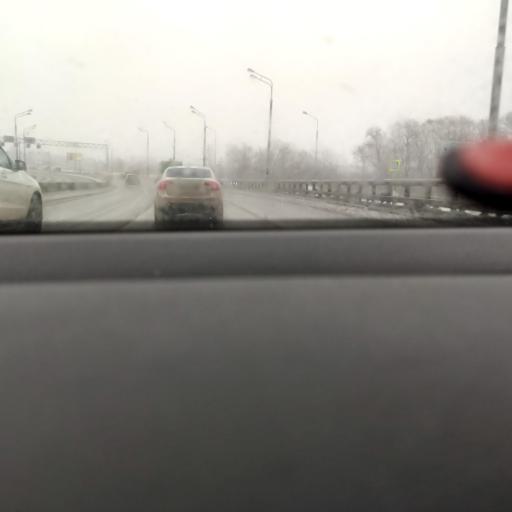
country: RU
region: Moskovskaya
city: Fili
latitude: 55.7530
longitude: 37.4528
